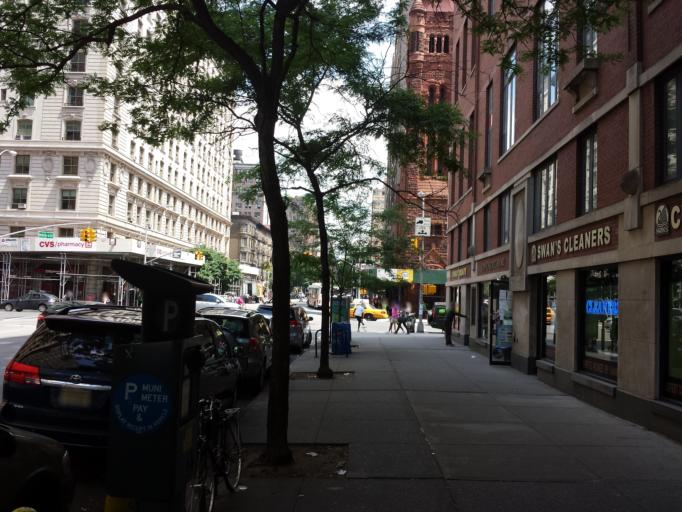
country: US
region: New York
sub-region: New York County
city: Manhattan
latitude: 40.7874
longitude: -73.9753
